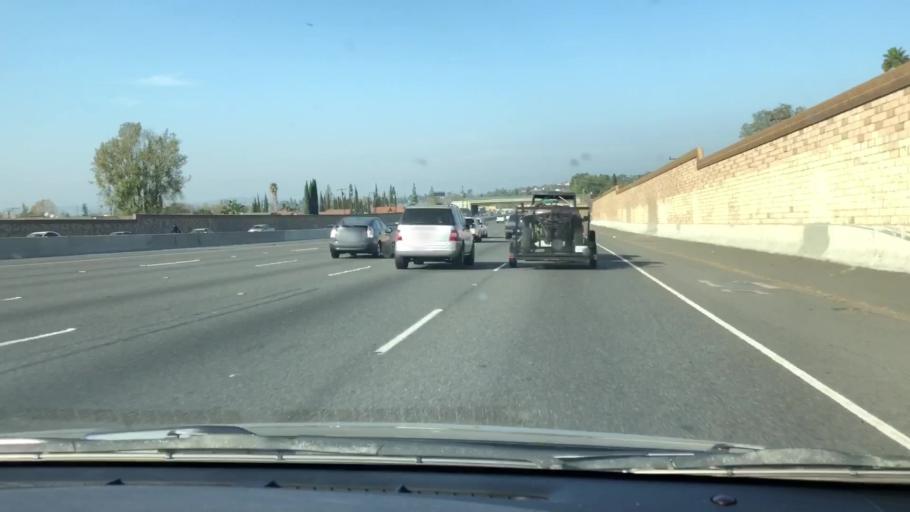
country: US
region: California
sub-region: Orange County
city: Villa Park
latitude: 33.8189
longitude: -117.8316
